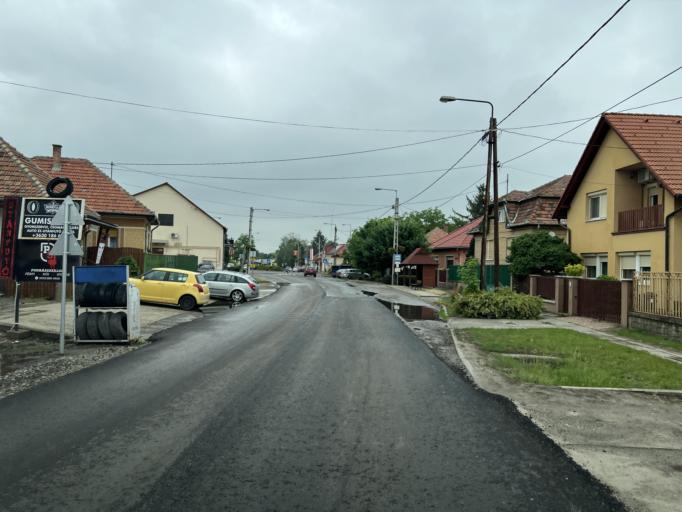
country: HU
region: Pest
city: Tura
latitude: 47.6091
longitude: 19.6024
